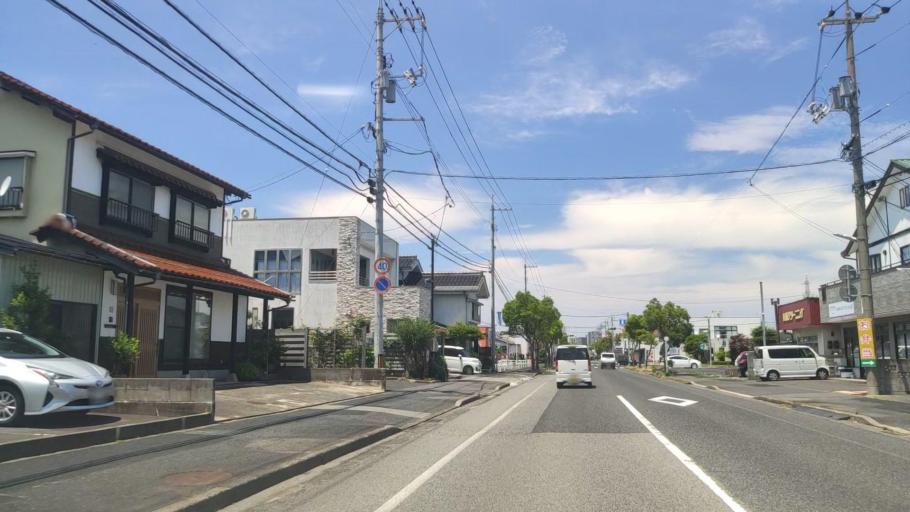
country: JP
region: Tottori
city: Tottori
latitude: 35.4793
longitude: 134.2355
